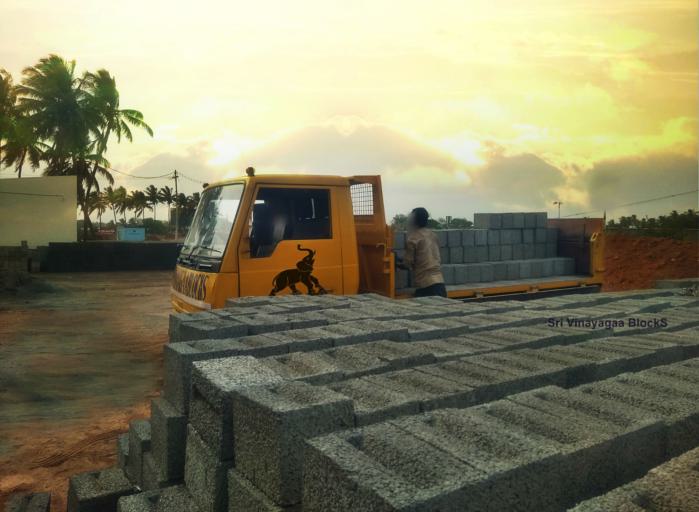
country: IN
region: Tamil Nadu
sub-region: Coimbatore
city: Sulur
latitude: 11.0251
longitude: 77.1723
